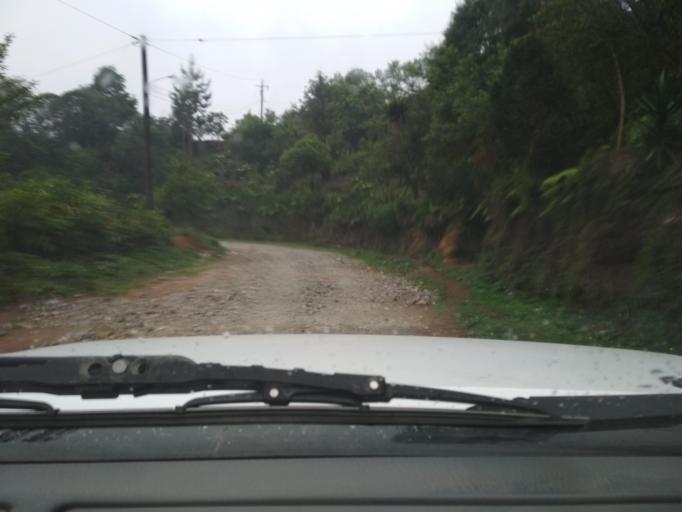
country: MX
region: Veracruz
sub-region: La Perla
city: Metlac Hernandez (Metlac Primero)
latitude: 18.9583
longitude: -97.1272
